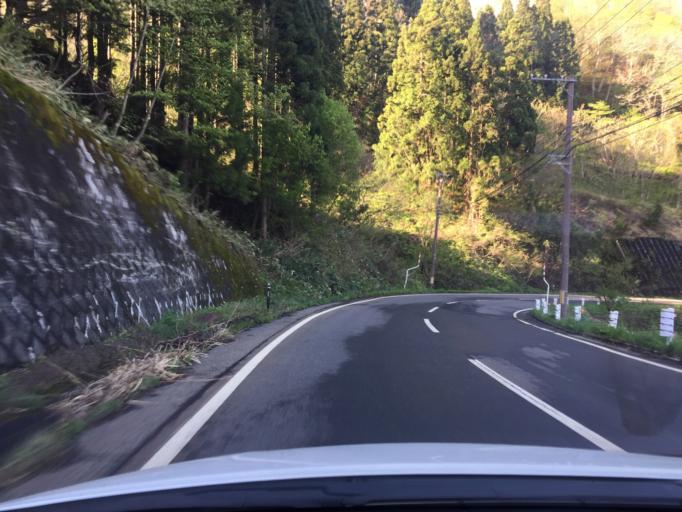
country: JP
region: Fukushima
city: Kitakata
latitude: 37.6629
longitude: 140.0083
